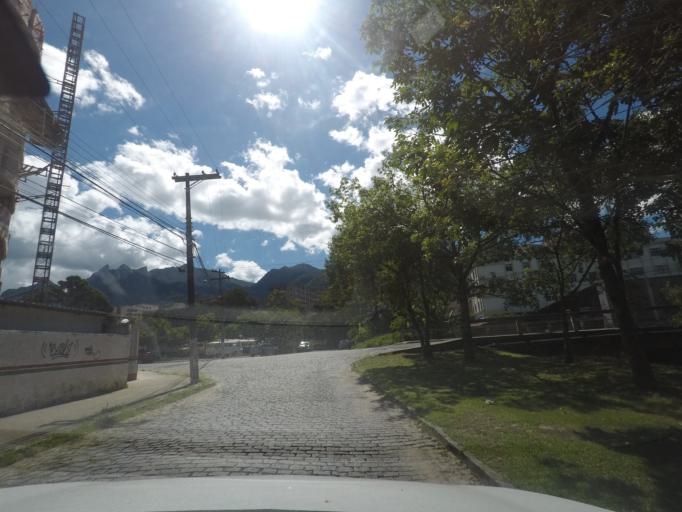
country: BR
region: Rio de Janeiro
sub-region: Teresopolis
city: Teresopolis
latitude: -22.4366
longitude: -42.9763
